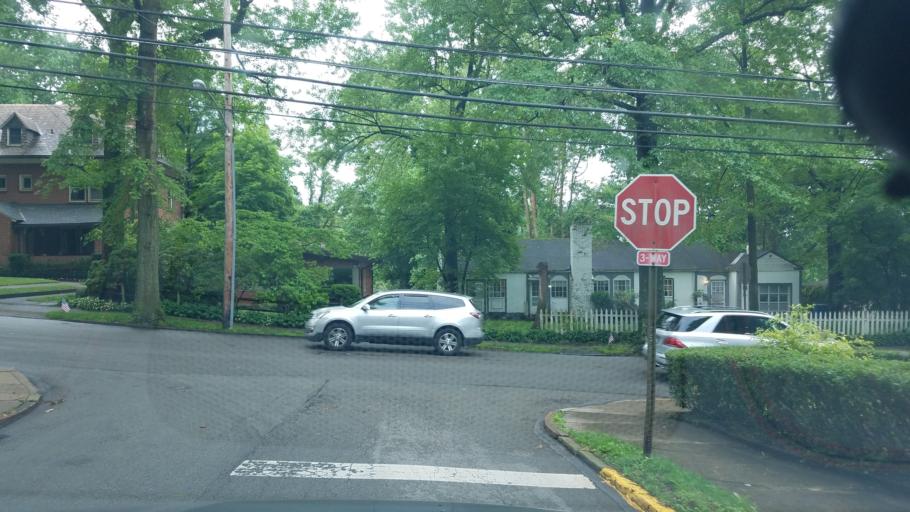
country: US
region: Pennsylvania
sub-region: Allegheny County
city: Edgewood
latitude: 40.4304
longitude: -79.8770
